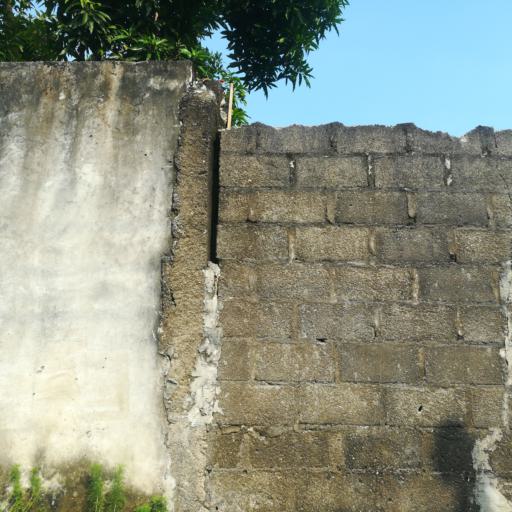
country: NG
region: Rivers
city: Port Harcourt
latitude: 4.8563
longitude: 6.9617
